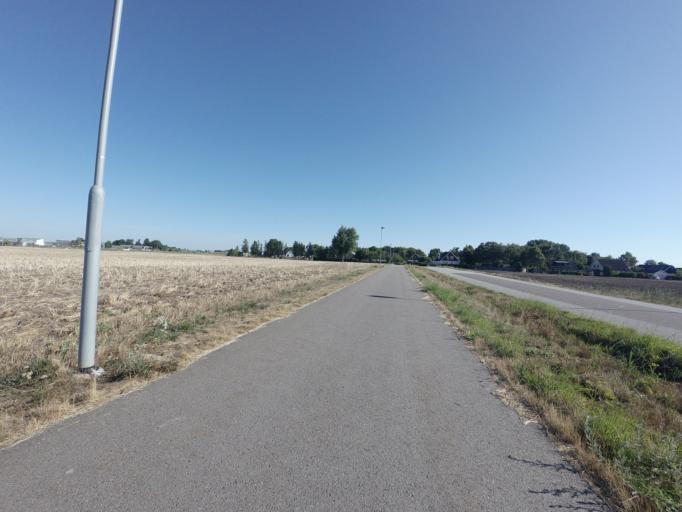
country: SE
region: Skane
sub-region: Trelleborgs Kommun
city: Skare
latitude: 55.4027
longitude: 13.0909
